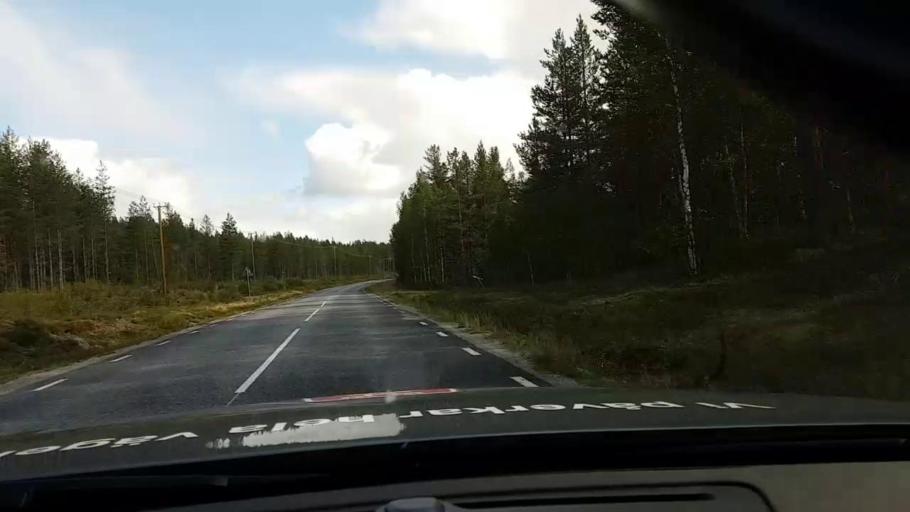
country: SE
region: Vaesterbotten
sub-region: Asele Kommun
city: Asele
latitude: 63.8481
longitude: 17.4069
